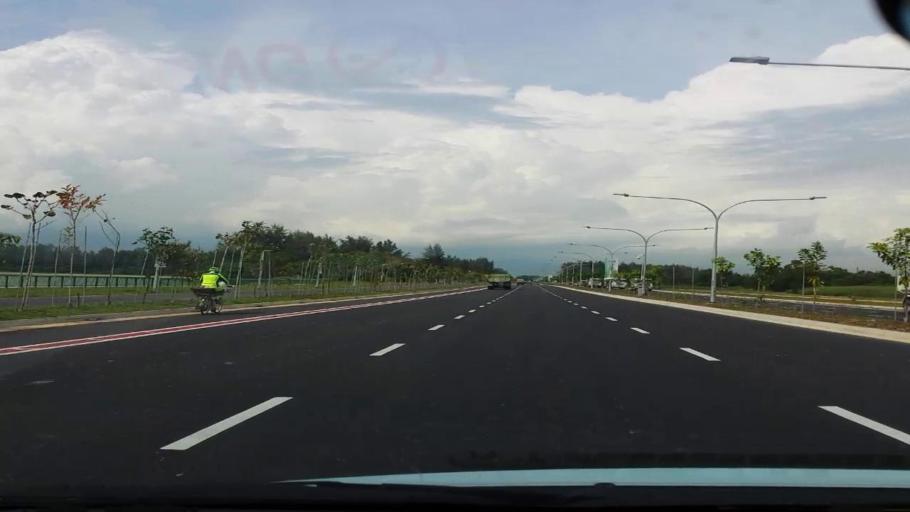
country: SG
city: Singapore
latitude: 1.3341
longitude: 104.0224
